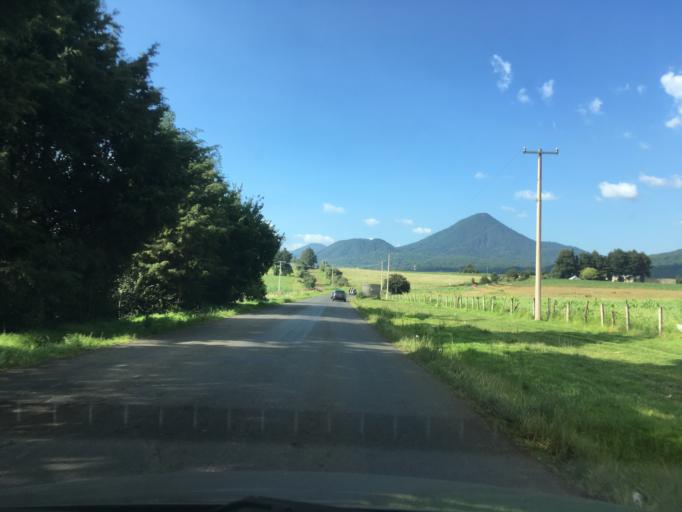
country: MX
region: Michoacan
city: Nahuatzen
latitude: 19.6436
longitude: -101.9236
